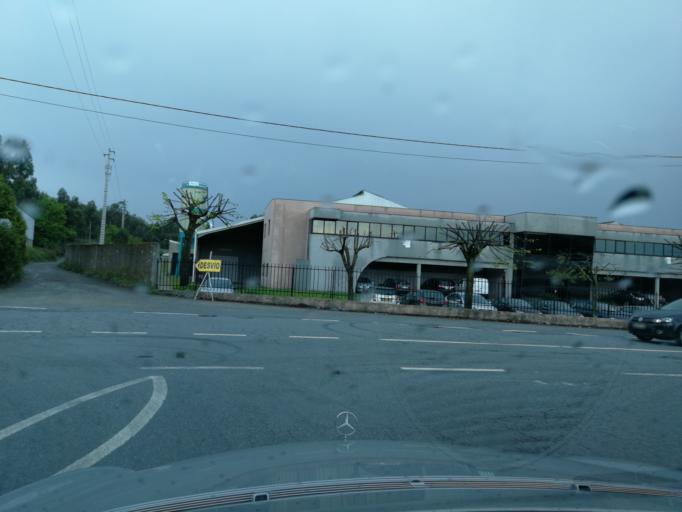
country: PT
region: Braga
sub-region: Vila Nova de Famalicao
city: Joane
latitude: 41.4659
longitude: -8.4276
